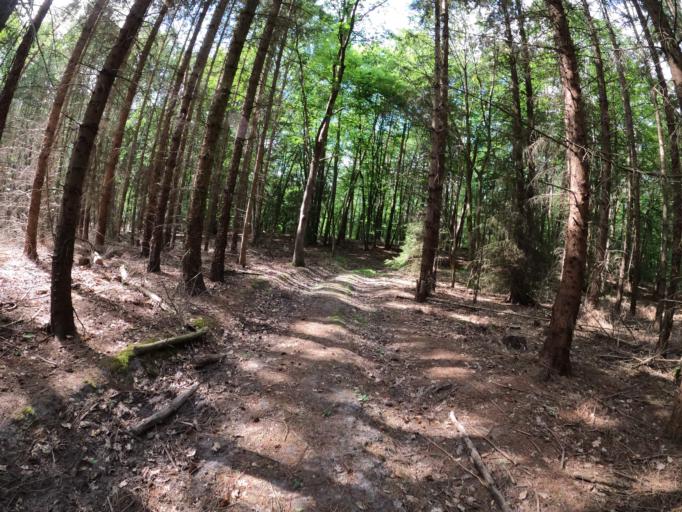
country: DE
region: Brandenburg
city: Angermunde
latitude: 53.0298
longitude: 13.9279
